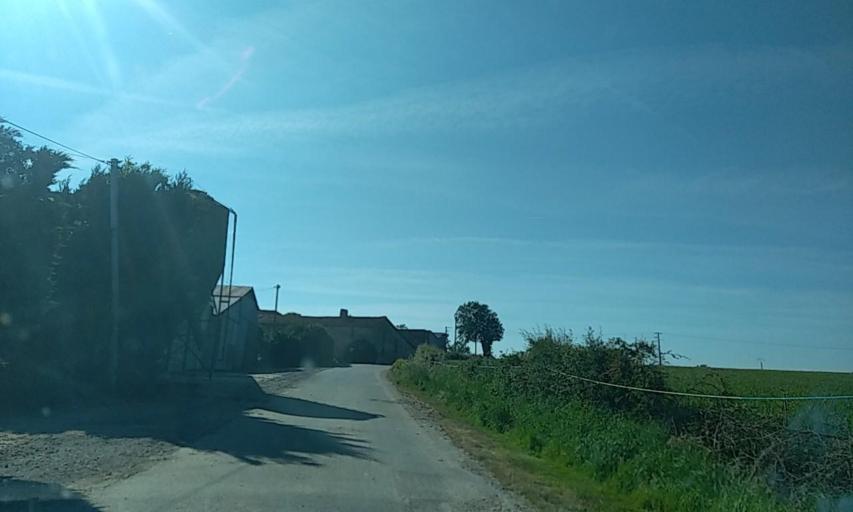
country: FR
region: Poitou-Charentes
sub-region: Departement des Deux-Sevres
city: Boisme
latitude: 46.8022
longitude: -0.4259
